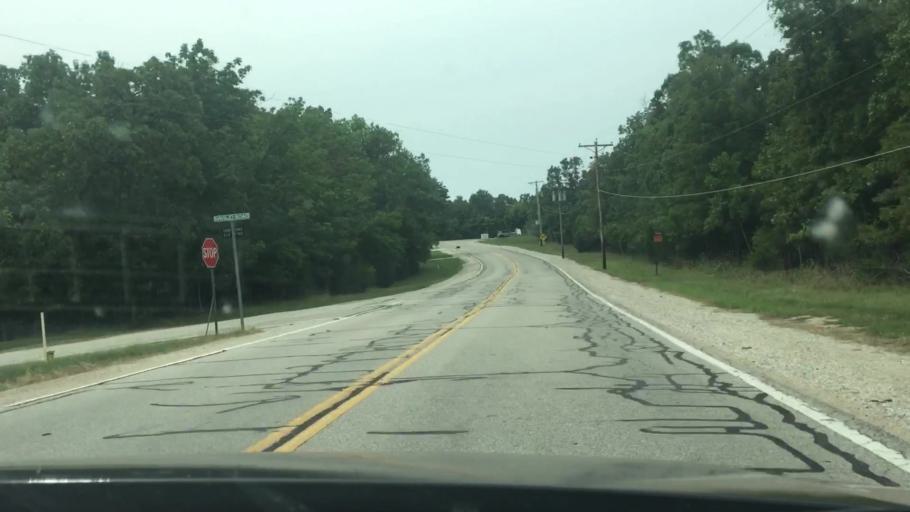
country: US
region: Missouri
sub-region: Camden County
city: Four Seasons
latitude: 38.2032
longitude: -92.7029
